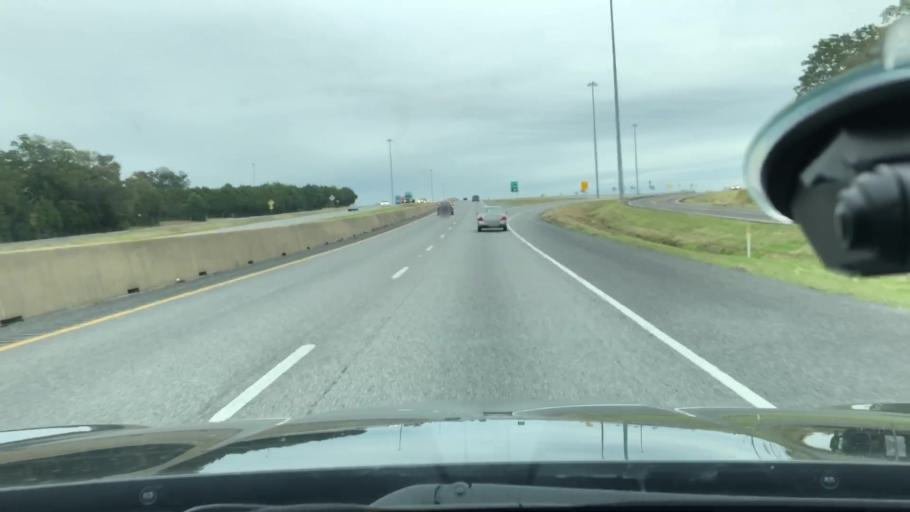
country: US
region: Texas
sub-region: Hunt County
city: Greenville
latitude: 33.1296
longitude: -95.9983
